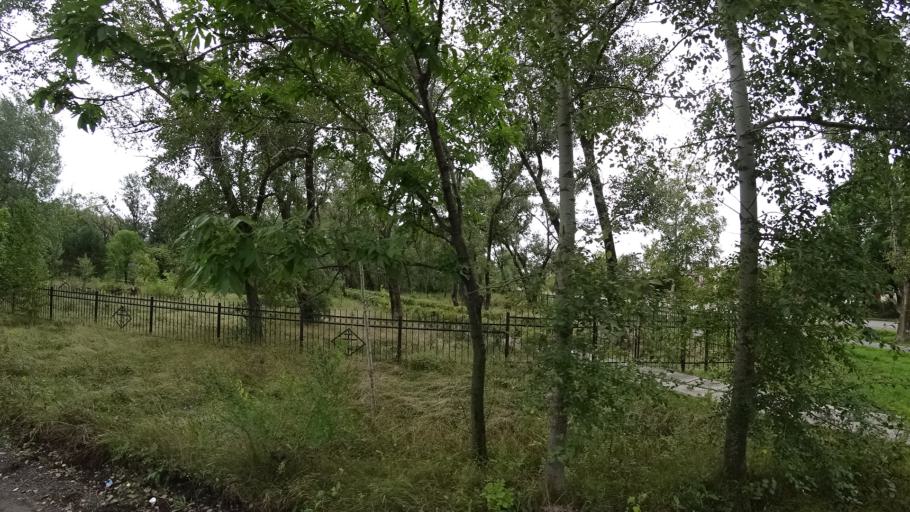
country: RU
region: Primorskiy
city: Chernigovka
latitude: 44.3409
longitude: 132.5798
